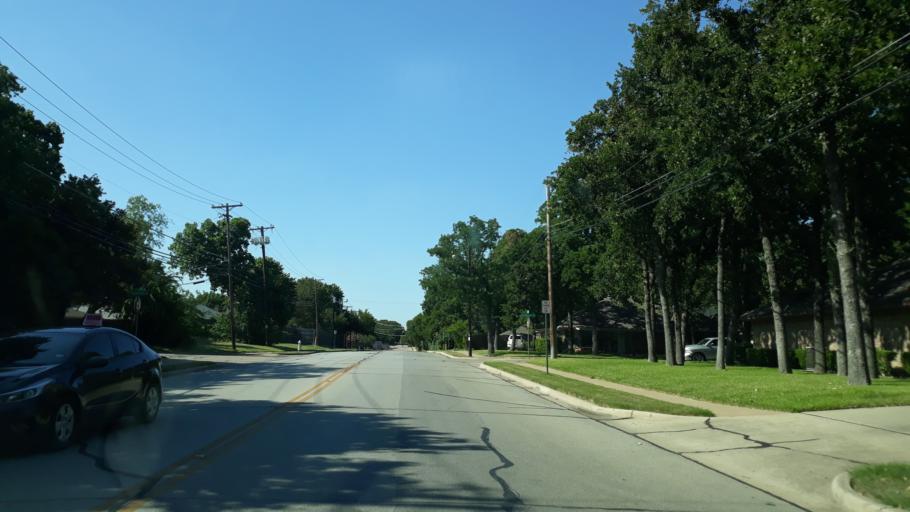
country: US
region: Texas
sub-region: Dallas County
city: Irving
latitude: 32.8270
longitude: -97.0044
